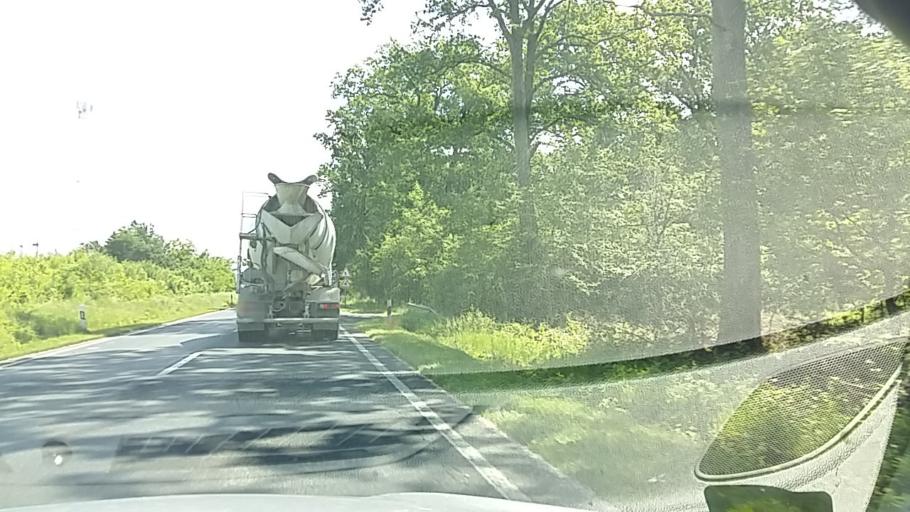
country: AT
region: Burgenland
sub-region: Politischer Bezirk Gussing
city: Moschendorf
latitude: 46.9773
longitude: 16.4977
